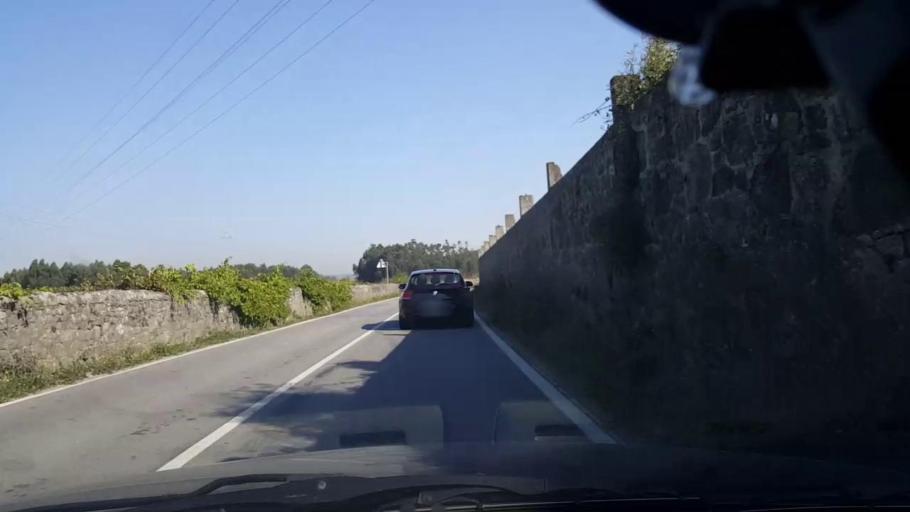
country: PT
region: Porto
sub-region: Vila do Conde
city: Arvore
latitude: 41.3262
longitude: -8.6817
